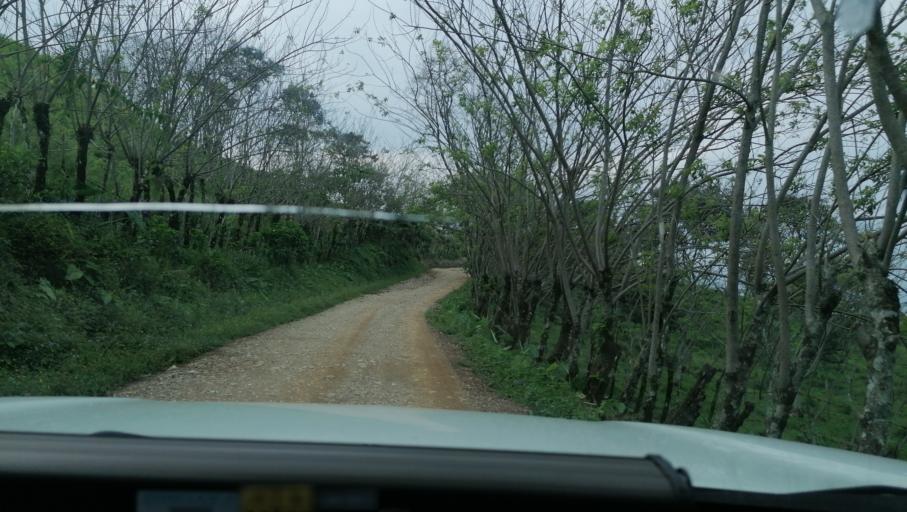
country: MX
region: Chiapas
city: Ixtacomitan
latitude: 17.3379
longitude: -93.1138
